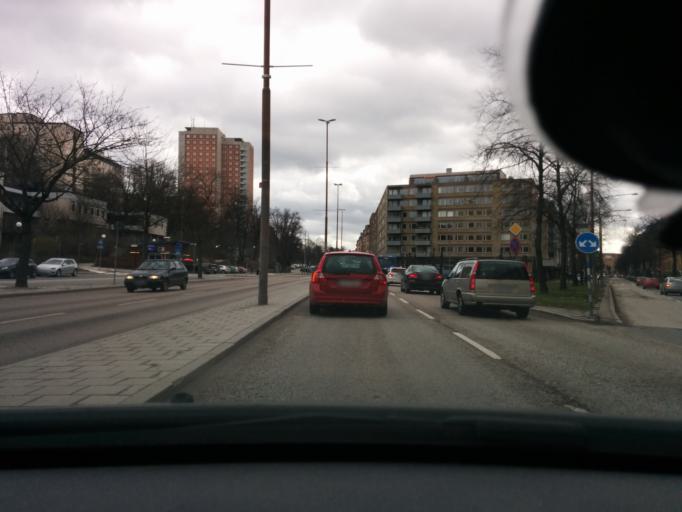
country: SE
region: Stockholm
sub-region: Stockholms Kommun
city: Stockholm
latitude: 59.3507
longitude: 18.0579
